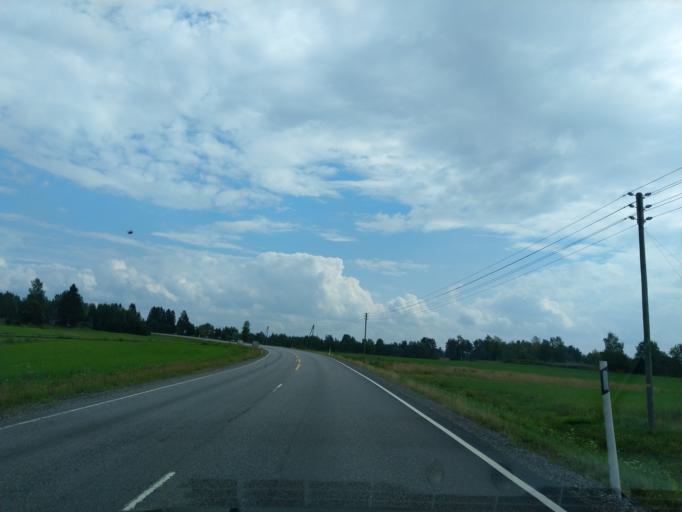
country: FI
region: South Karelia
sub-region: Imatra
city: Parikkala
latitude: 61.6053
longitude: 29.4639
